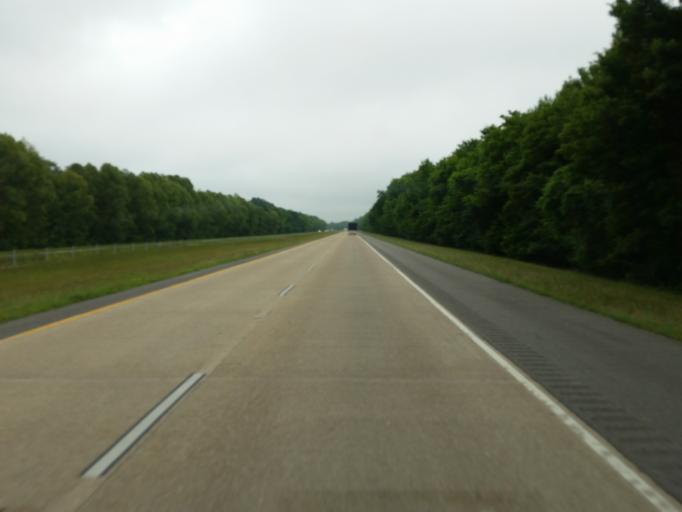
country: US
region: Louisiana
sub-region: Madison Parish
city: Tallulah
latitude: 32.3443
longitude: -91.0786
